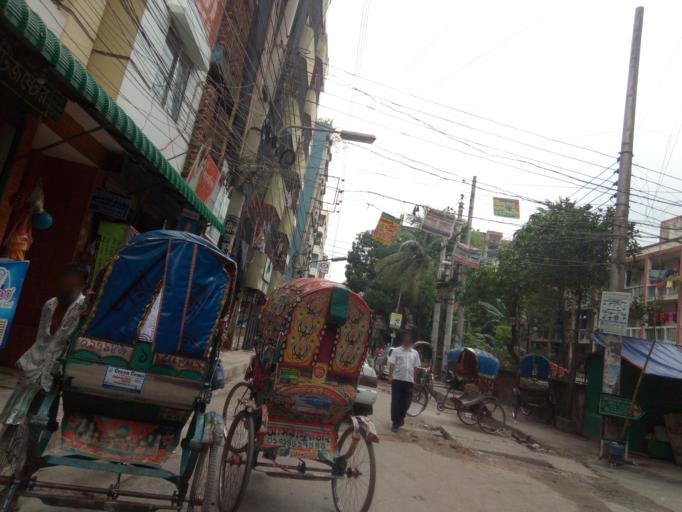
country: BD
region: Dhaka
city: Azimpur
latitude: 23.7683
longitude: 90.3601
